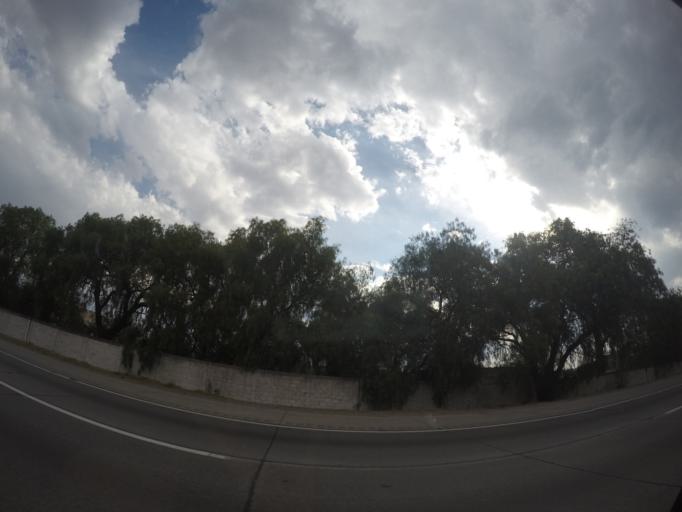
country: MX
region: Hidalgo
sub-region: Tepeji del Rio de Ocampo
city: Santiago Tlautla
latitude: 19.9688
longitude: -99.4285
